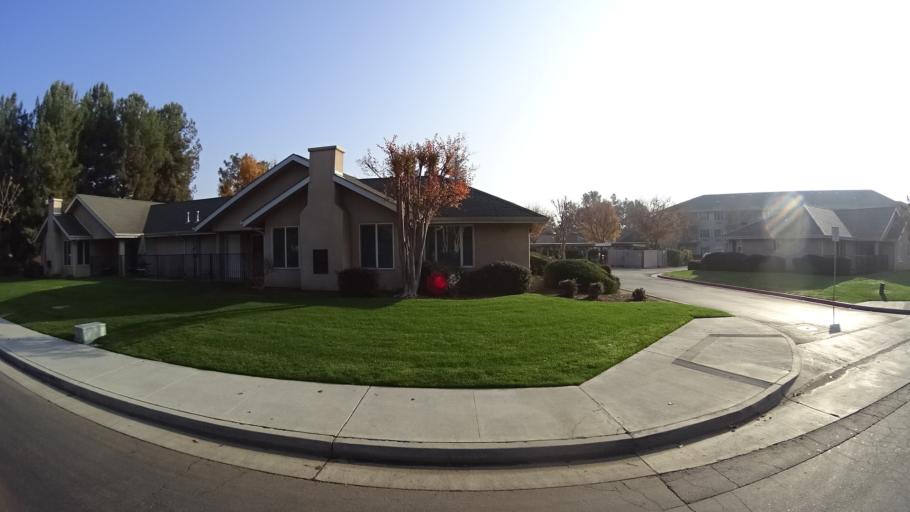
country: US
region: California
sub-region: Kern County
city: Greenacres
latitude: 35.3315
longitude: -119.0953
